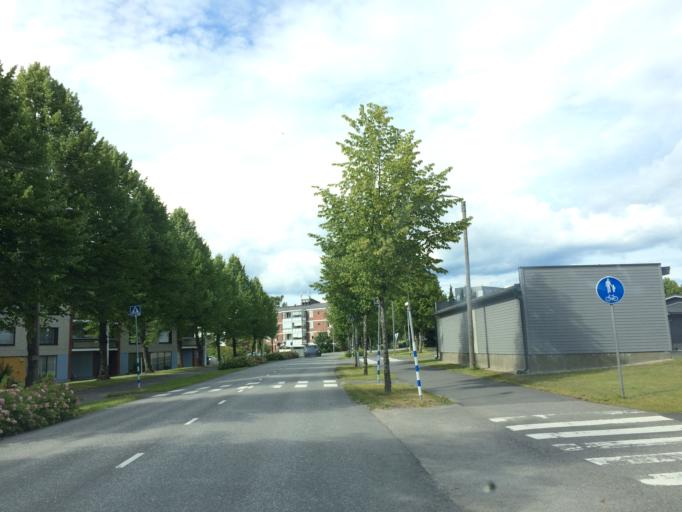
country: FI
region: Haeme
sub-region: Haemeenlinna
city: Turenki
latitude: 60.9223
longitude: 24.6454
